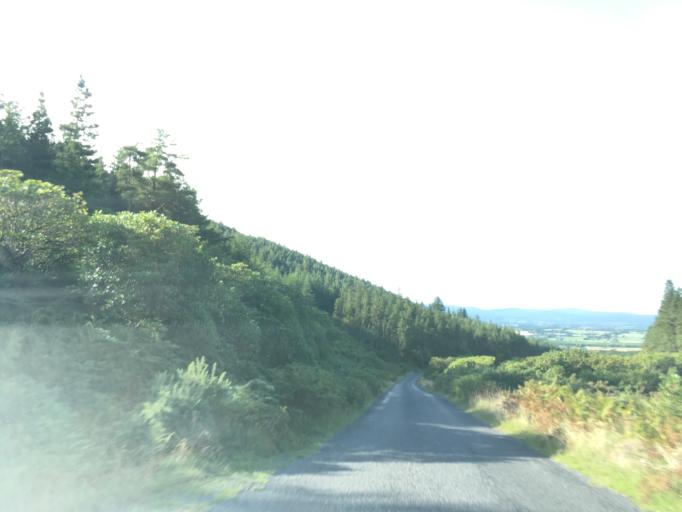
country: IE
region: Munster
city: Cahir
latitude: 52.2547
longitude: -7.9607
